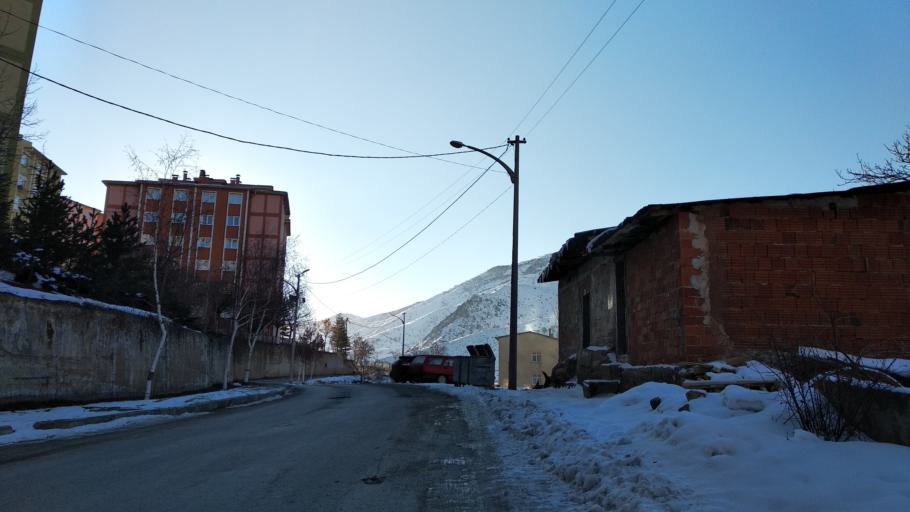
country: TR
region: Gumushane
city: Gumushkhane
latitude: 40.4379
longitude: 39.5083
